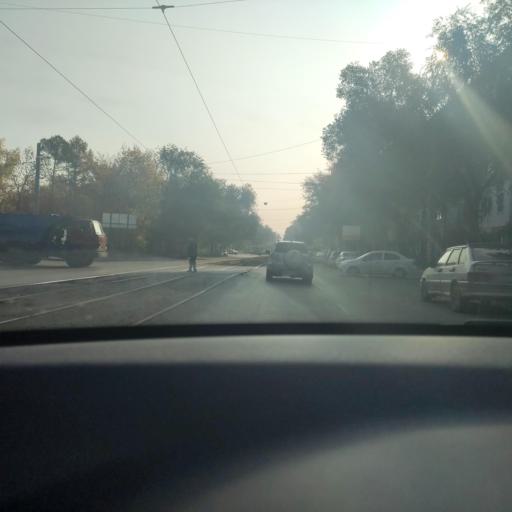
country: RU
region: Samara
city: Petra-Dubrava
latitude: 53.2403
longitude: 50.2776
